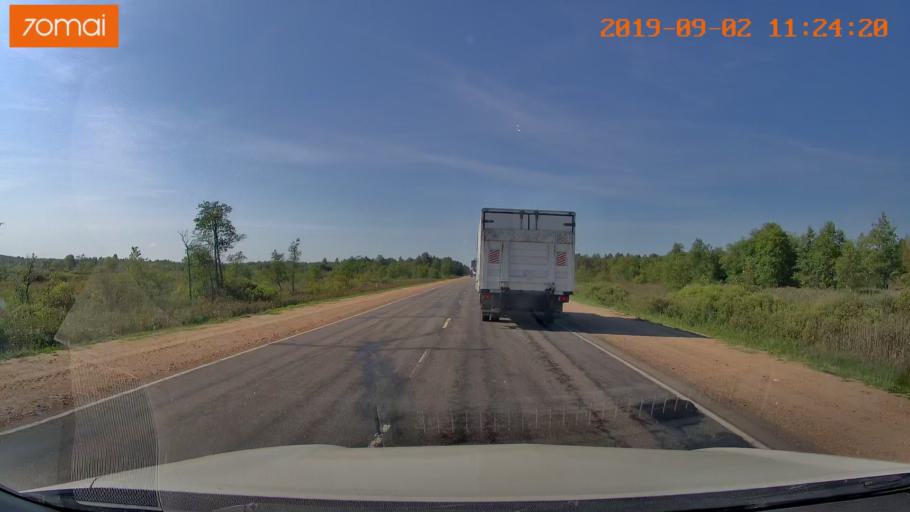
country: RU
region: Smolensk
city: Roslavl'
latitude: 54.0112
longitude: 32.9772
